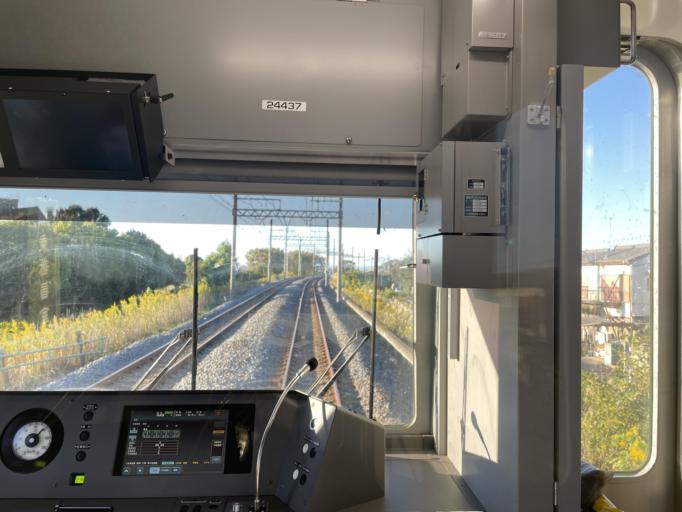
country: JP
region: Saitama
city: Kurihashi
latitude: 36.1289
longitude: 139.6946
